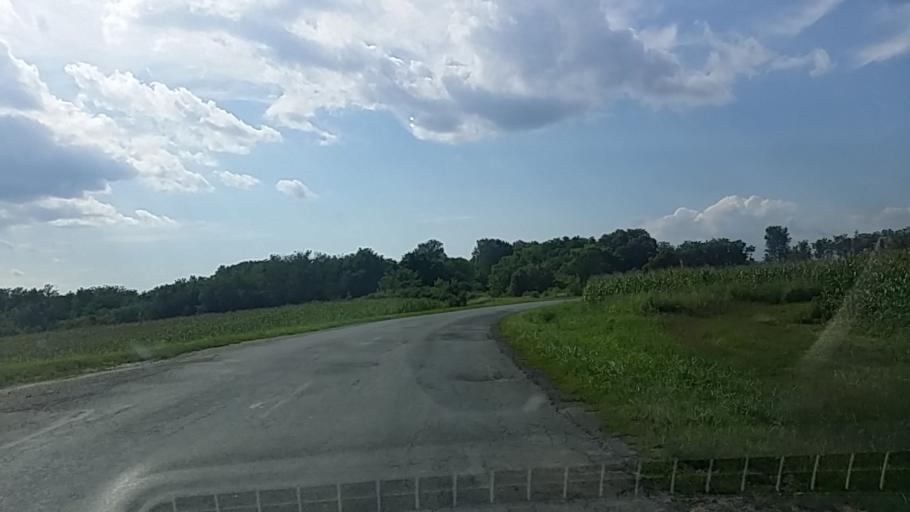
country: HU
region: Zala
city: Becsehely
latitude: 46.5191
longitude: 16.7706
